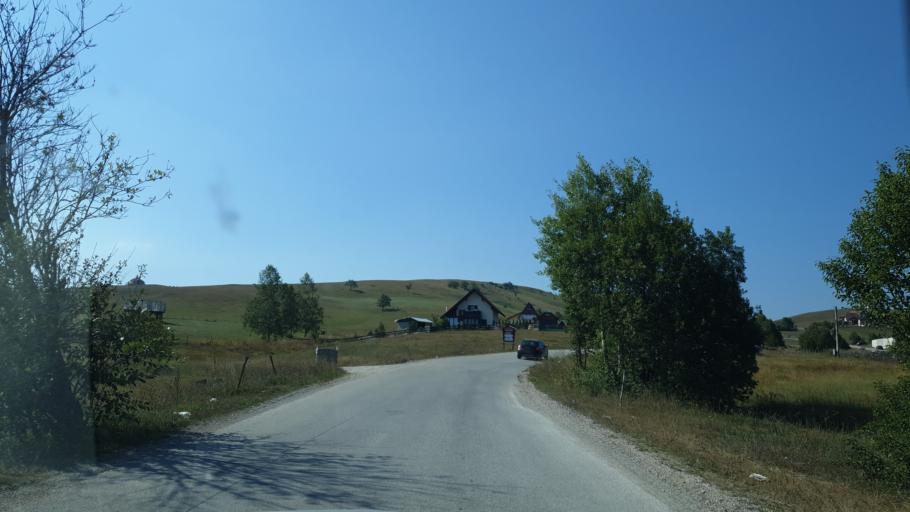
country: RS
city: Zlatibor
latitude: 43.7167
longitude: 19.7359
